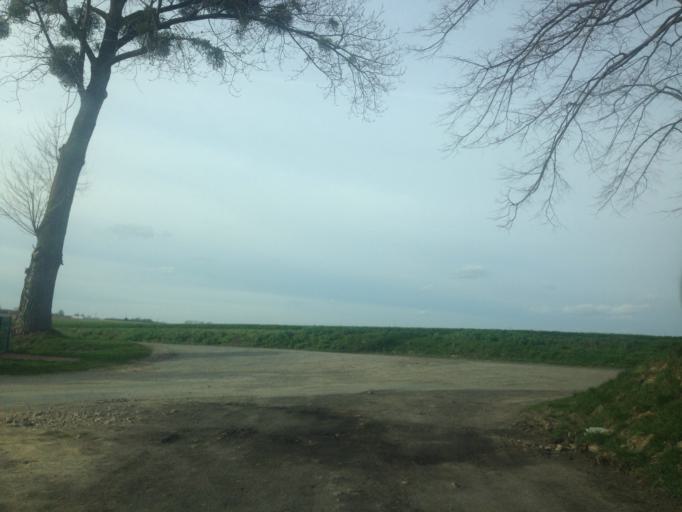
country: PL
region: Kujawsko-Pomorskie
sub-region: Powiat brodnicki
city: Jablonowo Pomorskie
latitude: 53.3848
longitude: 19.2385
